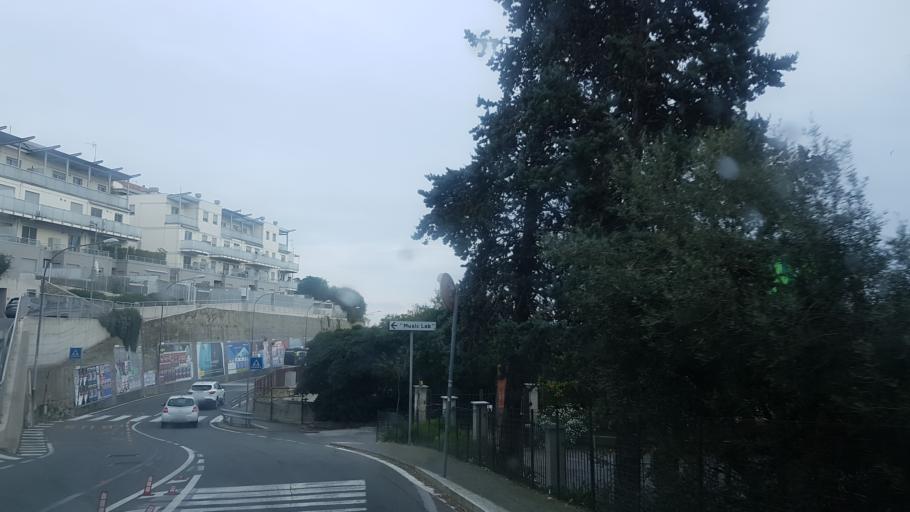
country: IT
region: Liguria
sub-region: Provincia di Savona
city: Savona
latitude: 44.3013
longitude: 8.4622
